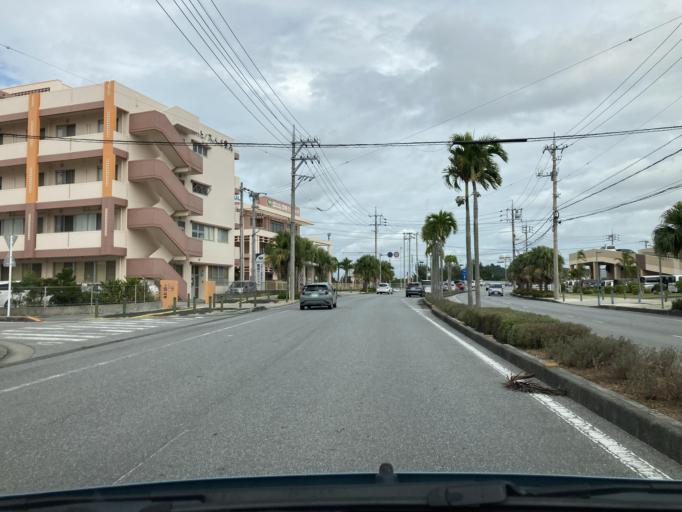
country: JP
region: Okinawa
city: Tomigusuku
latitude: 26.1596
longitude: 127.6599
